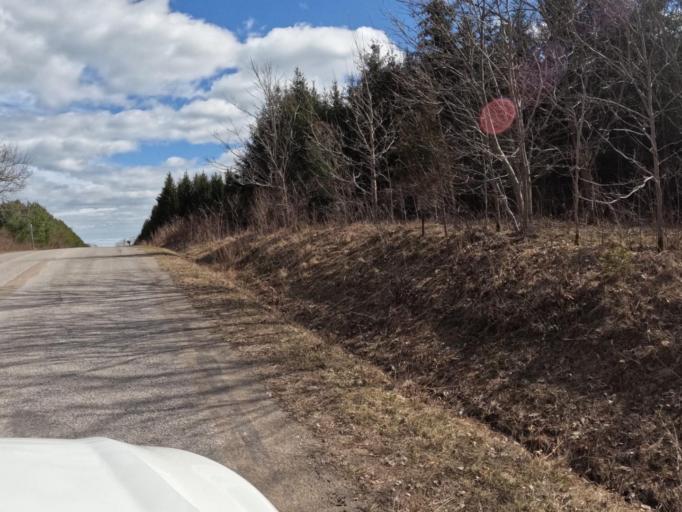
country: CA
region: Ontario
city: Norfolk County
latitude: 42.7538
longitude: -80.2767
